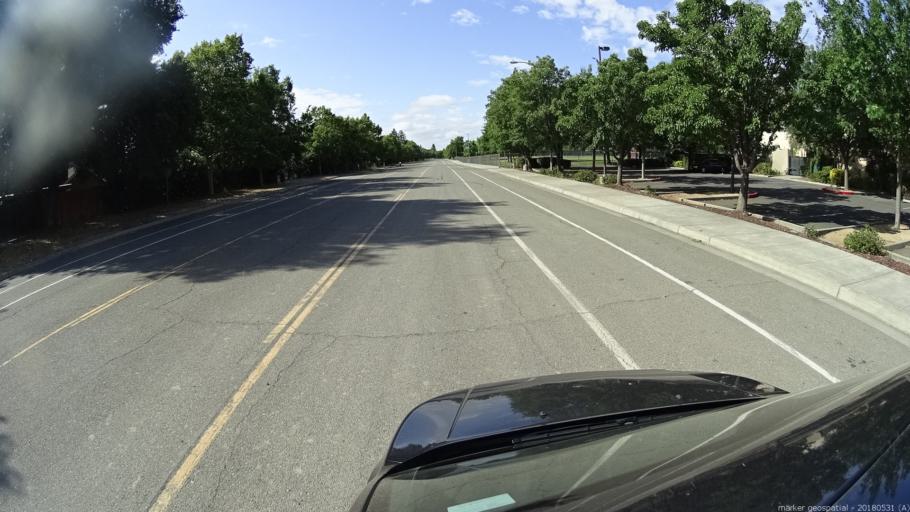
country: US
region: California
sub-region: Sacramento County
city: Sacramento
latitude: 38.6333
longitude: -121.4935
